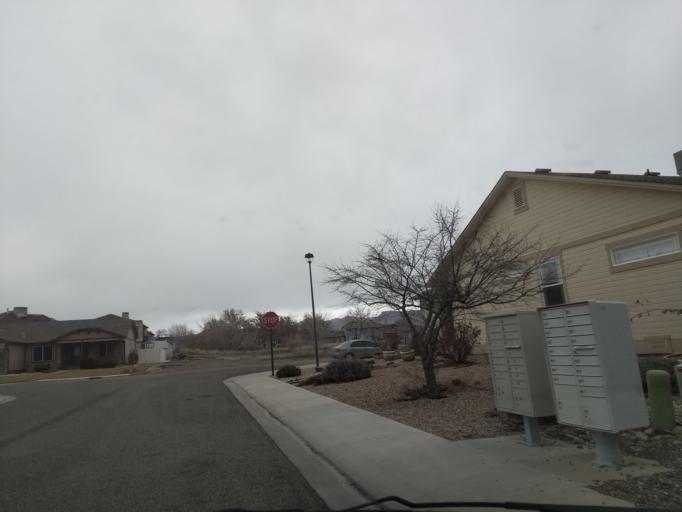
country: US
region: Colorado
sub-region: Mesa County
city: Fruitvale
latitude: 39.0878
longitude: -108.5198
